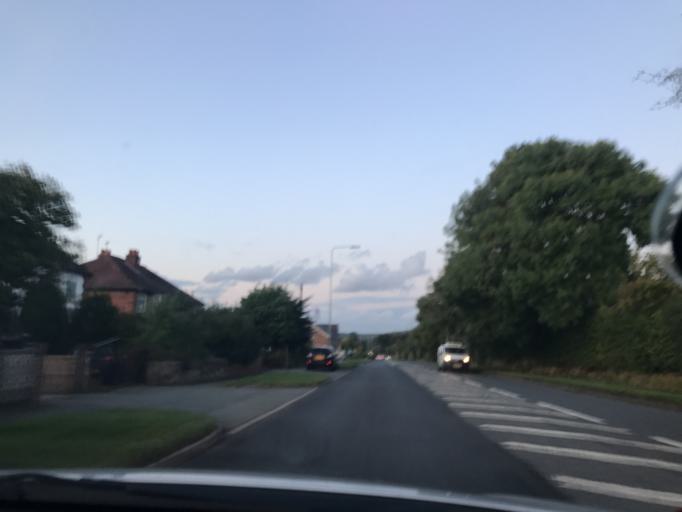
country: GB
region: England
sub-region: Cheshire West and Chester
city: Tarvin
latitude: 53.1977
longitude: -2.7679
